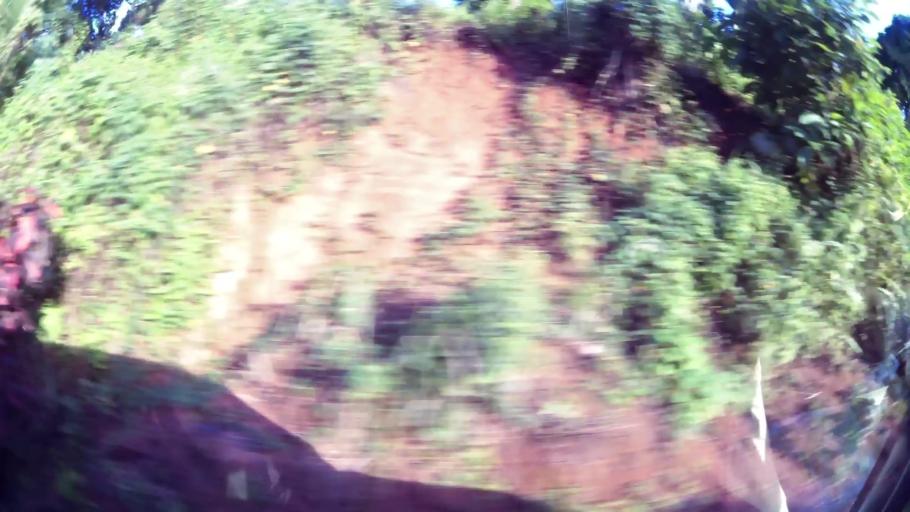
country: DM
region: Saint John
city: Portsmouth
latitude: 15.5785
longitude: -61.4205
